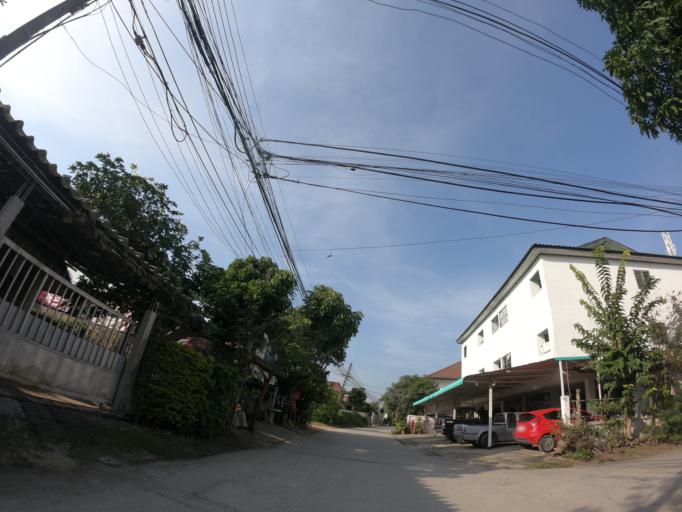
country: TH
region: Chiang Mai
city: Chiang Mai
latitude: 18.8280
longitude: 98.9882
